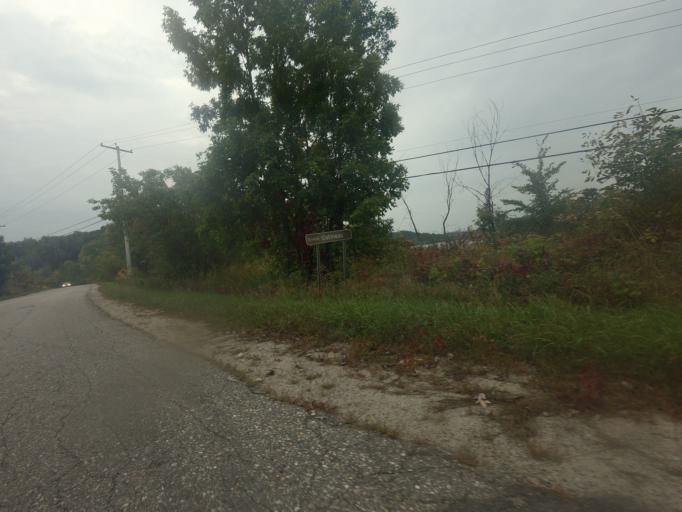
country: CA
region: Quebec
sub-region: Outaouais
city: Maniwaki
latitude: 46.0898
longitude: -76.0420
